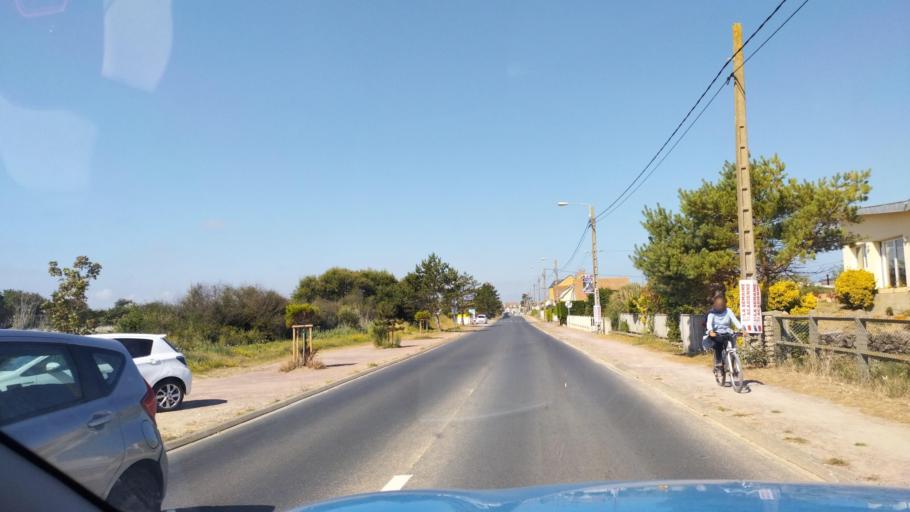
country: FR
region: Lower Normandy
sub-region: Departement du Calvados
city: Bernieres-sur-Mer
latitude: 49.3344
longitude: -0.4108
